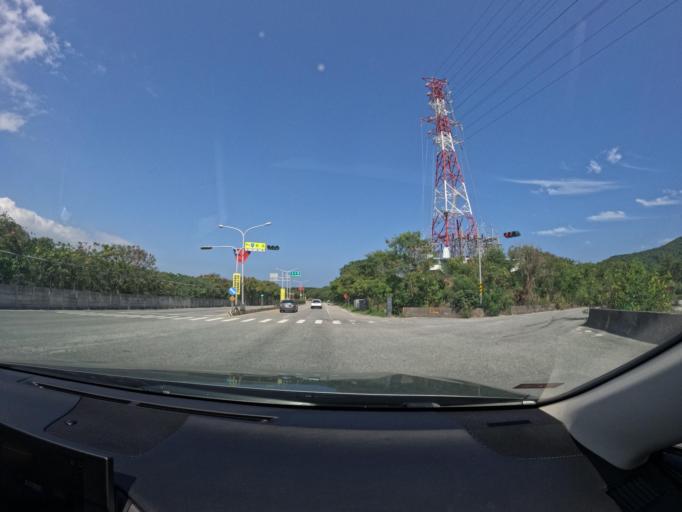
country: TW
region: Taiwan
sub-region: Hualien
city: Hualian
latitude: 23.9230
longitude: 121.5890
